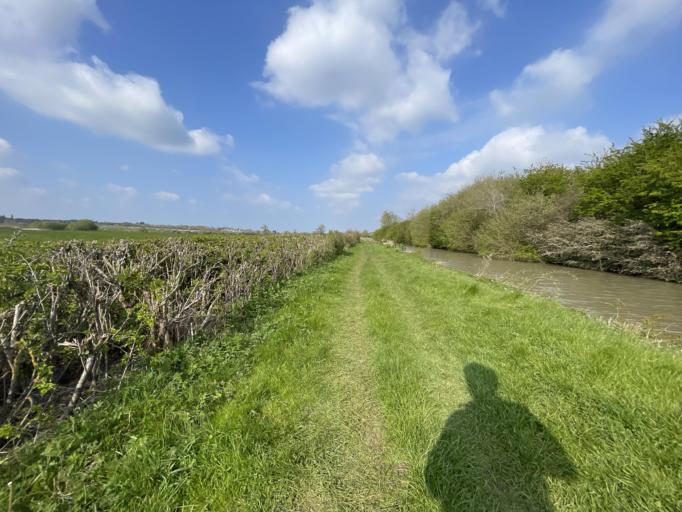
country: GB
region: England
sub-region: Warwickshire
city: Rugby
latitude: 52.3449
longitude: -1.2097
